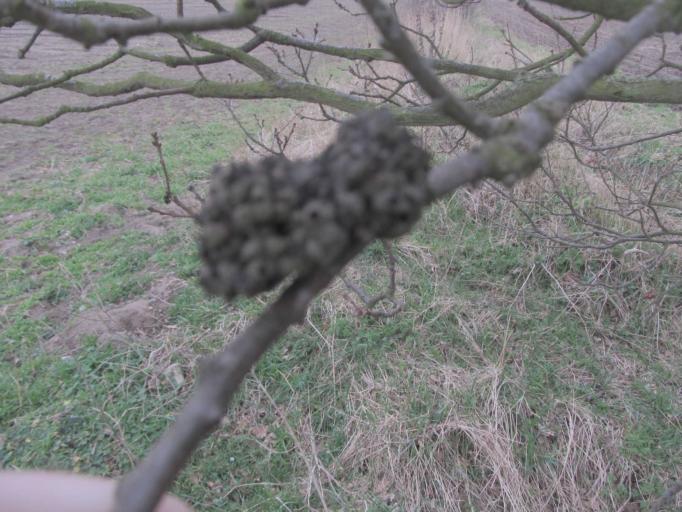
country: GB
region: England
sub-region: Doncaster
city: Bawtry
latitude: 53.4285
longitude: -0.9651
